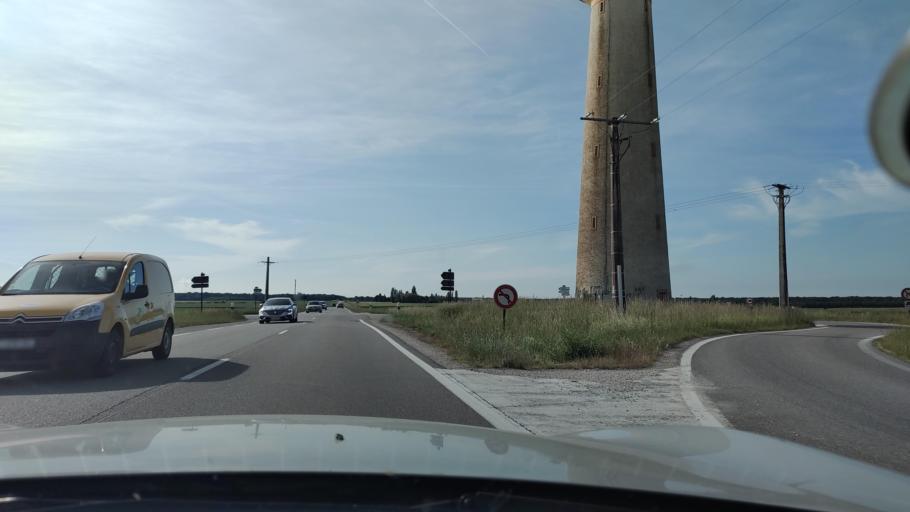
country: FR
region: Ile-de-France
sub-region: Departement de Seine-et-Marne
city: Jouy-le-Chatel
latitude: 48.6562
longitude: 3.1483
